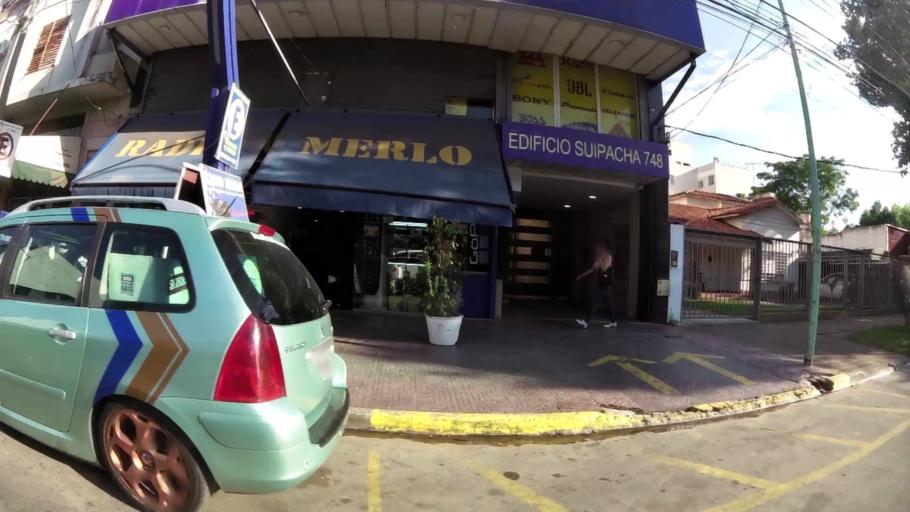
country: AR
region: Buenos Aires
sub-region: Partido de Merlo
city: Merlo
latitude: -34.6671
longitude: -58.7284
